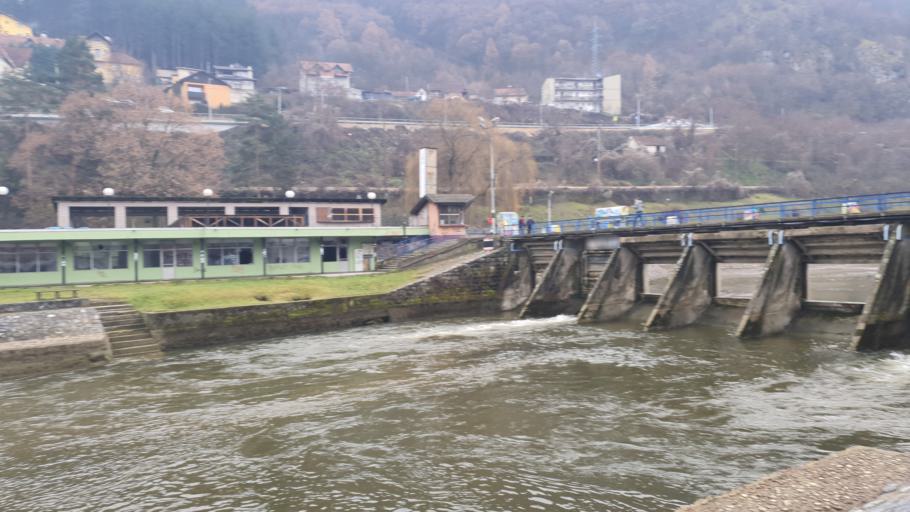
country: RS
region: Central Serbia
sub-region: Zlatiborski Okrug
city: Uzice
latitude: 43.8541
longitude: 19.8340
